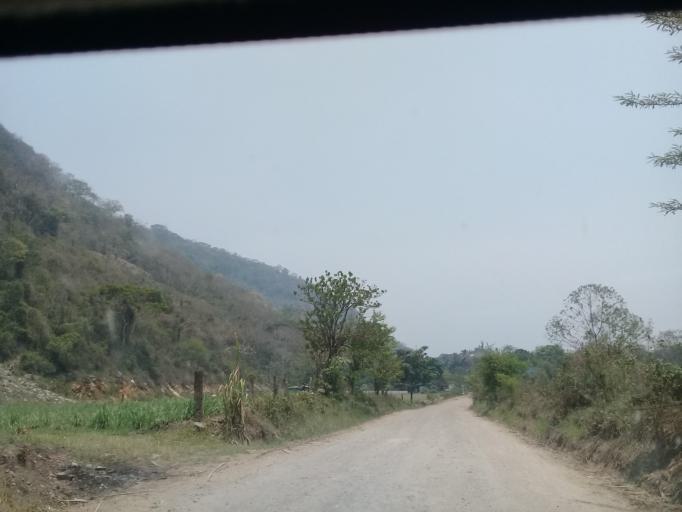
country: MX
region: Veracruz
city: Tezonapa
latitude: 18.6188
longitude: -96.6959
